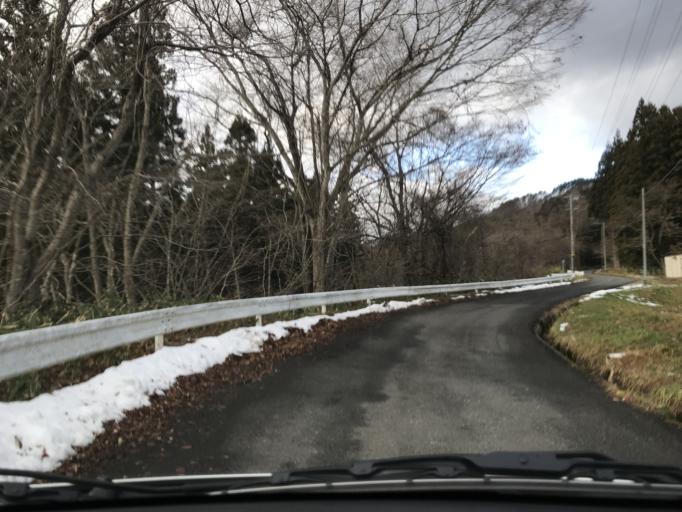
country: JP
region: Iwate
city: Ichinoseki
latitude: 39.0087
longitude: 140.9800
